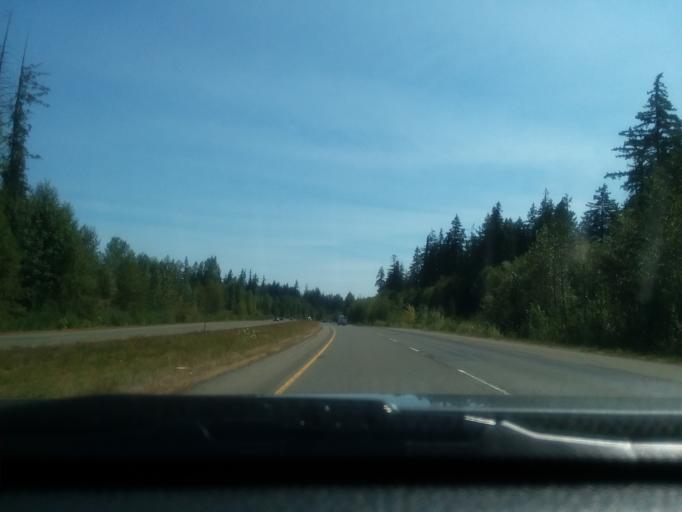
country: CA
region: British Columbia
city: Cumberland
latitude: 49.5055
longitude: -124.8466
